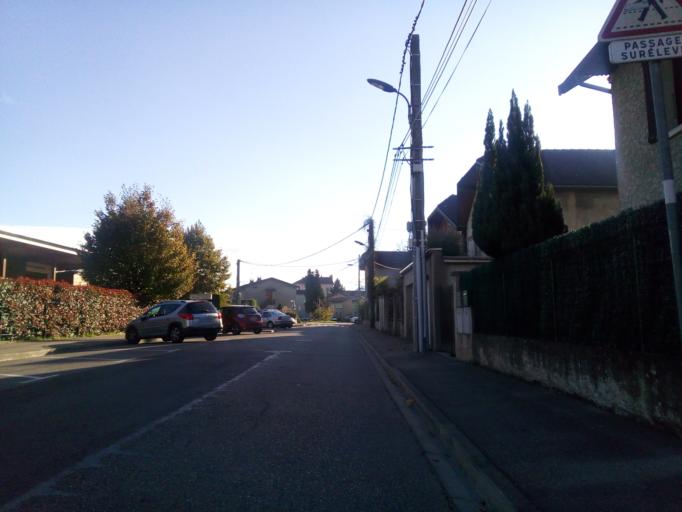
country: FR
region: Rhone-Alpes
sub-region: Departement de l'Isere
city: Saint-Martin-d'Heres
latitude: 45.1833
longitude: 5.7641
